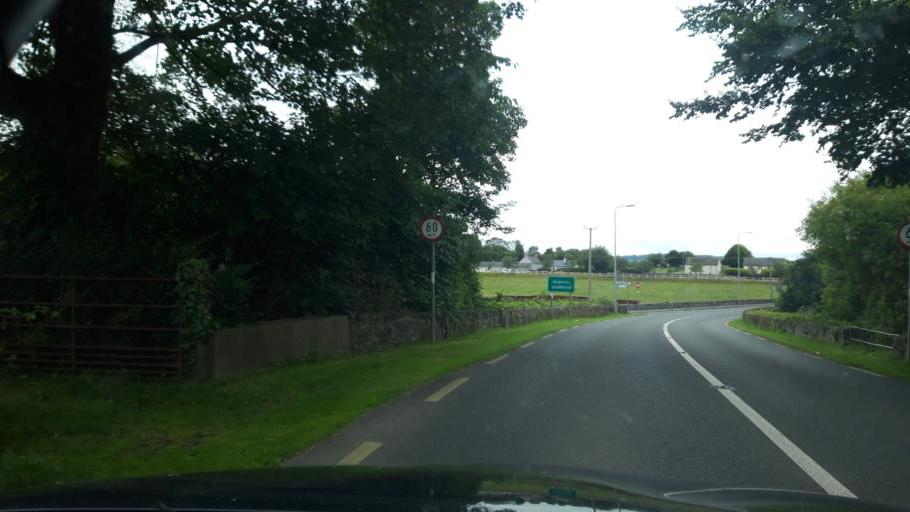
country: IE
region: Leinster
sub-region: Kilkenny
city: Thomastown
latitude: 52.6257
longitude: -7.0723
